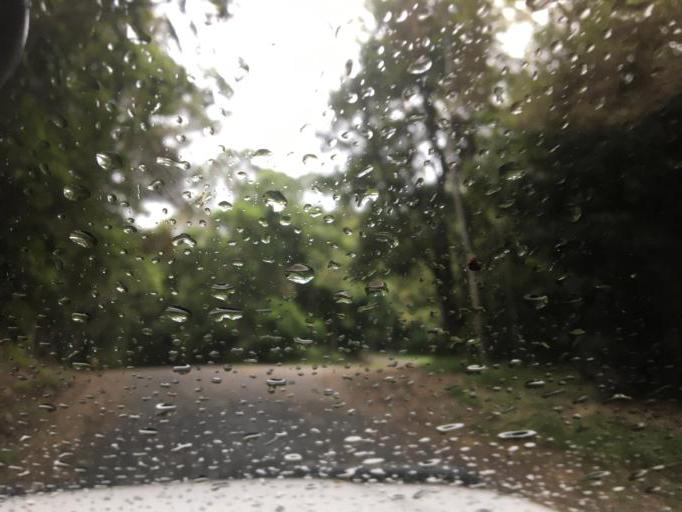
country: AU
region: Queensland
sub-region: Tablelands
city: Kuranda
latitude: -16.8451
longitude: 145.6429
